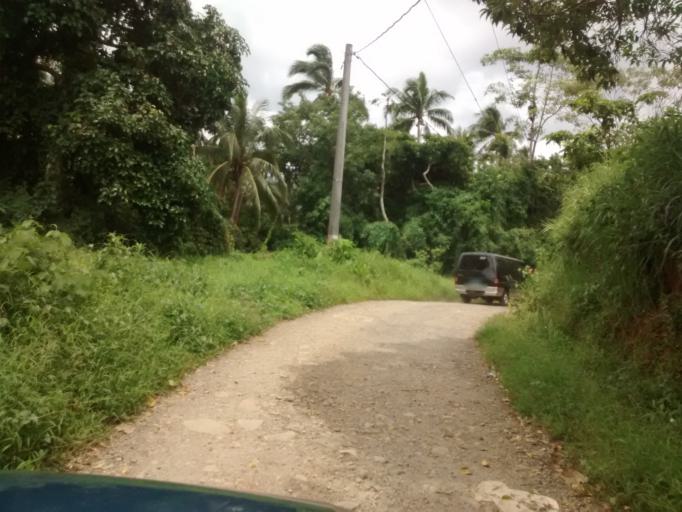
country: PH
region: Calabarzon
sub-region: Province of Quezon
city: Lucban
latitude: 14.1580
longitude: 121.5503
